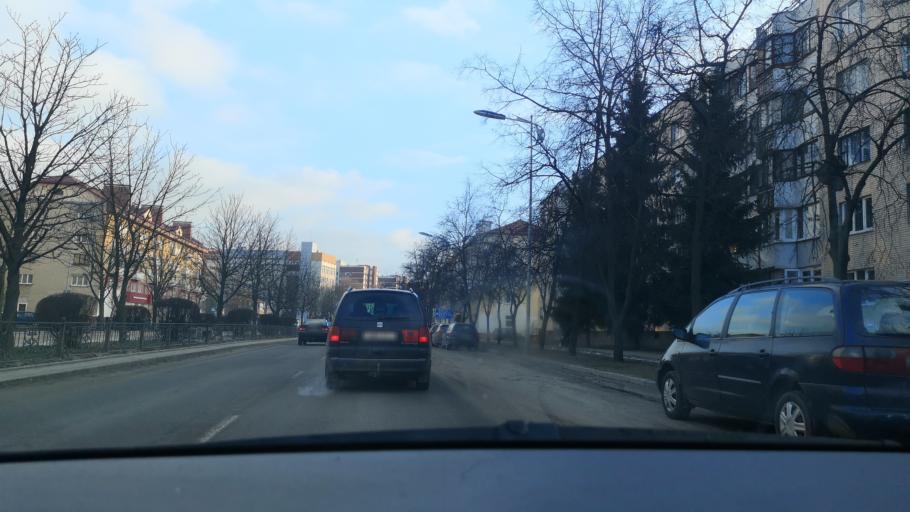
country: BY
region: Brest
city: Brest
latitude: 52.0955
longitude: 23.6980
